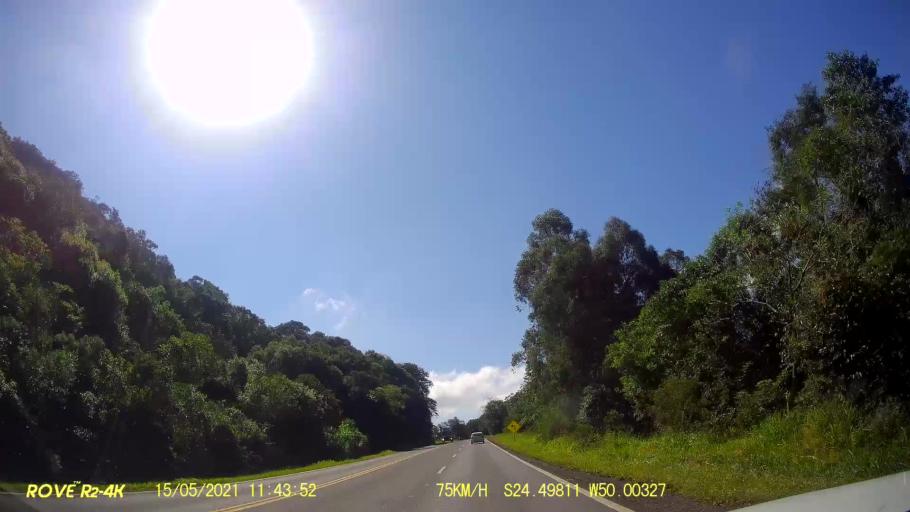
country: BR
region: Parana
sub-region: Pirai Do Sul
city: Pirai do Sul
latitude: -24.4981
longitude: -50.0033
